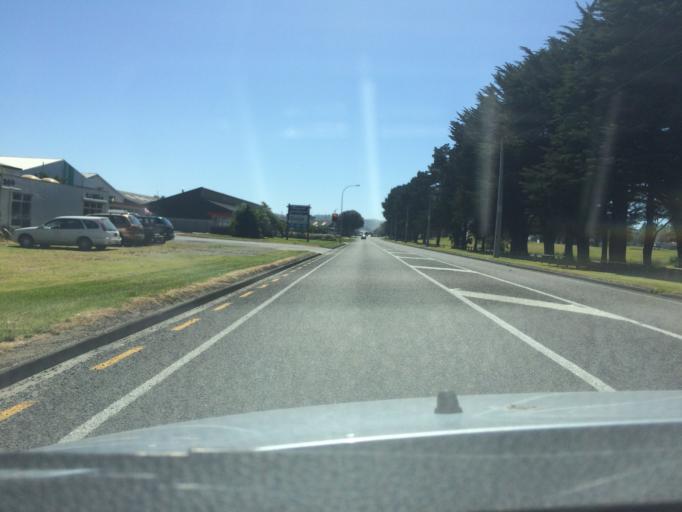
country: NZ
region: Gisborne
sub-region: Gisborne District
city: Gisborne
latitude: -38.6694
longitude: 177.9998
